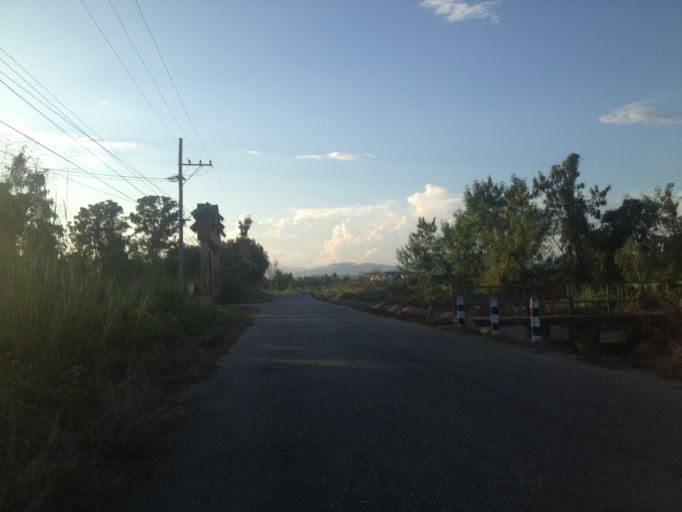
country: TH
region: Chiang Mai
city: San Pa Tong
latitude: 18.6482
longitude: 98.8933
